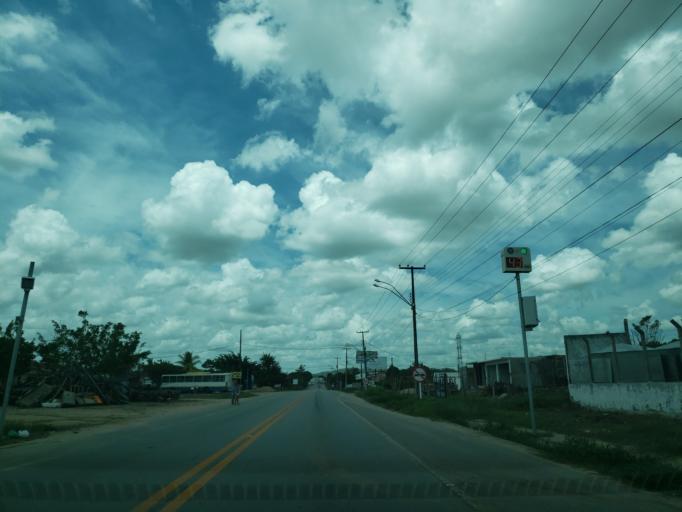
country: BR
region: Alagoas
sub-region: Uniao Dos Palmares
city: Uniao dos Palmares
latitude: -9.1618
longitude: -36.0172
